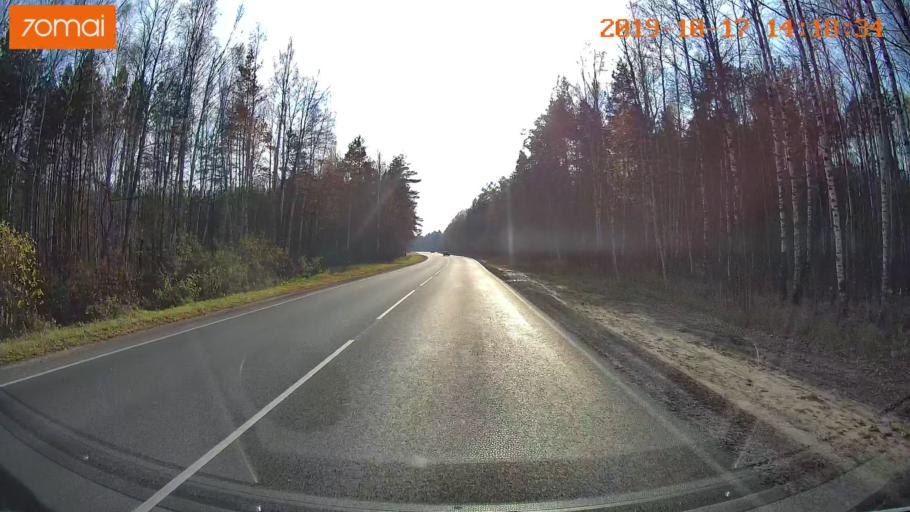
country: RU
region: Rjazan
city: Spas-Klepiki
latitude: 55.0615
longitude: 40.0289
